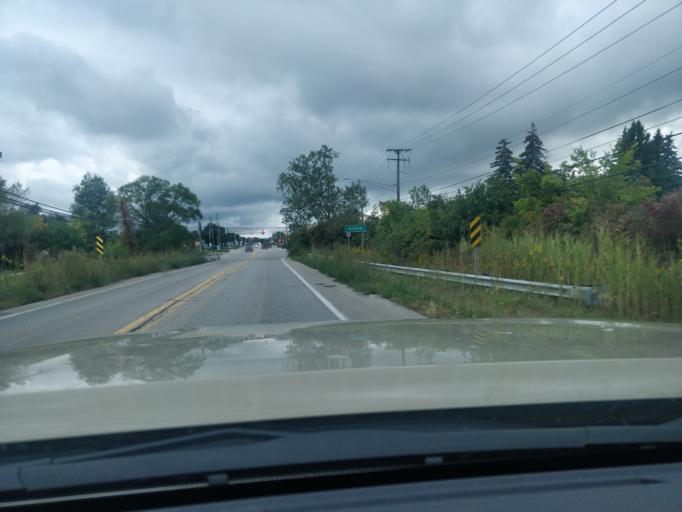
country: US
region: Michigan
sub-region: Wayne County
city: Woodhaven
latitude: 42.1697
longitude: -83.2247
